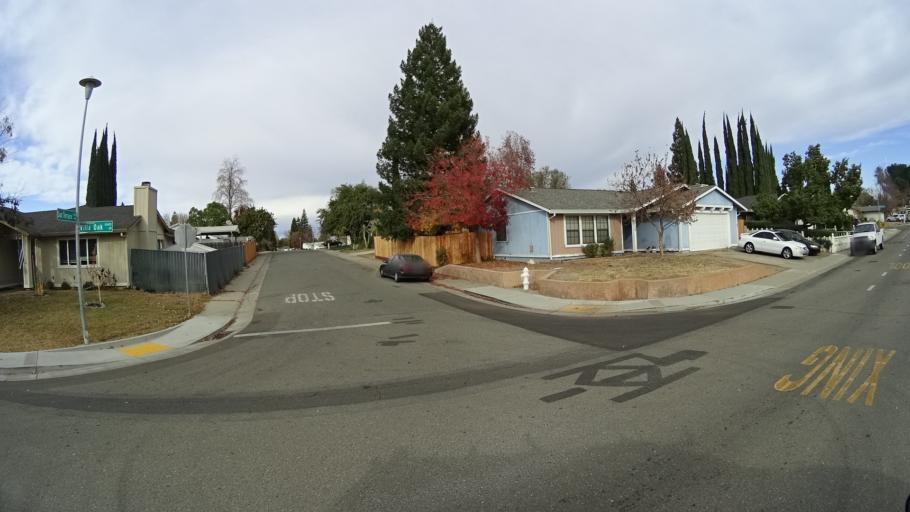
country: US
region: California
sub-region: Sacramento County
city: Citrus Heights
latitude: 38.7058
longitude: -121.2545
